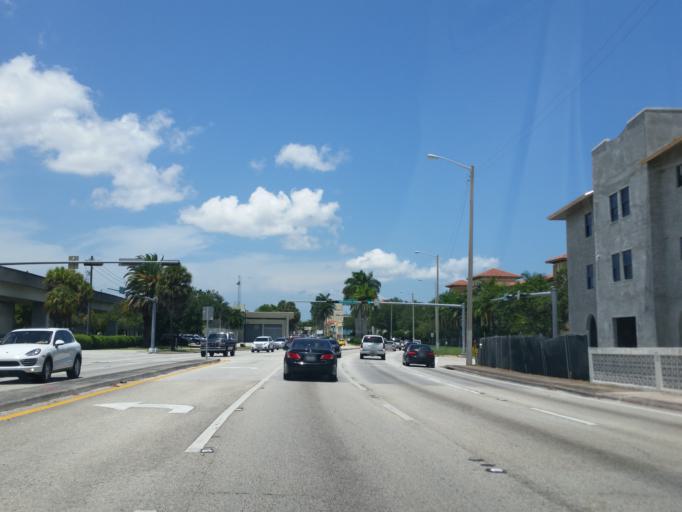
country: US
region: Florida
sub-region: Miami-Dade County
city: Coral Gables
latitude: 25.7232
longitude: -80.2662
